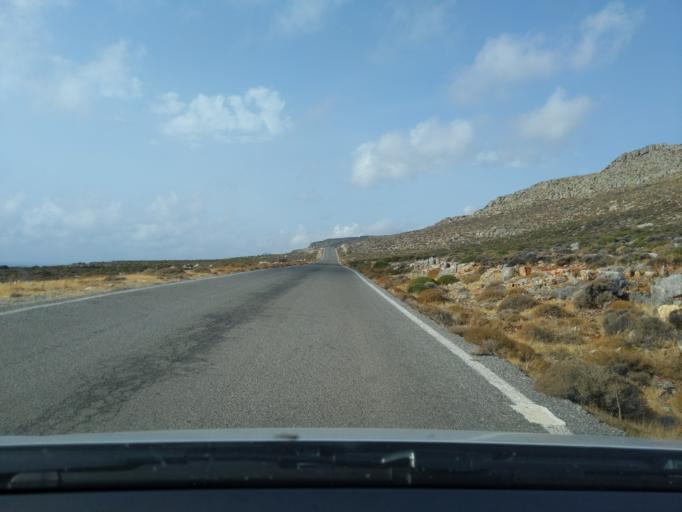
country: GR
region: Crete
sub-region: Nomos Lasithiou
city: Palekastro
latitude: 35.0865
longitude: 26.2655
